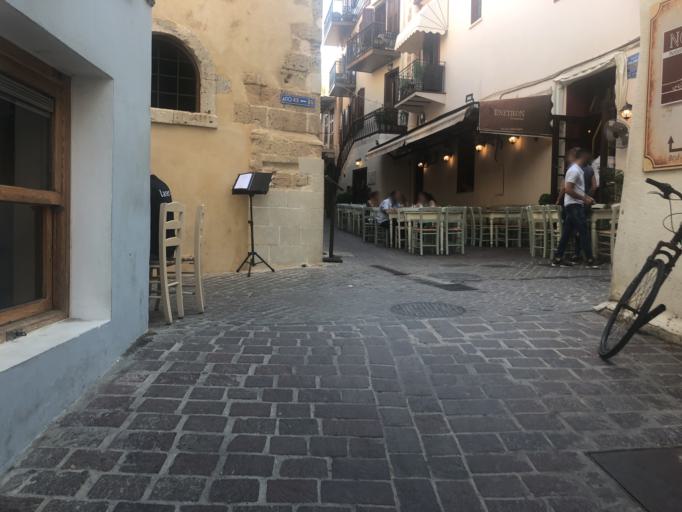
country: GR
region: Crete
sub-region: Nomos Chanias
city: Chania
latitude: 35.5166
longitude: 24.0163
